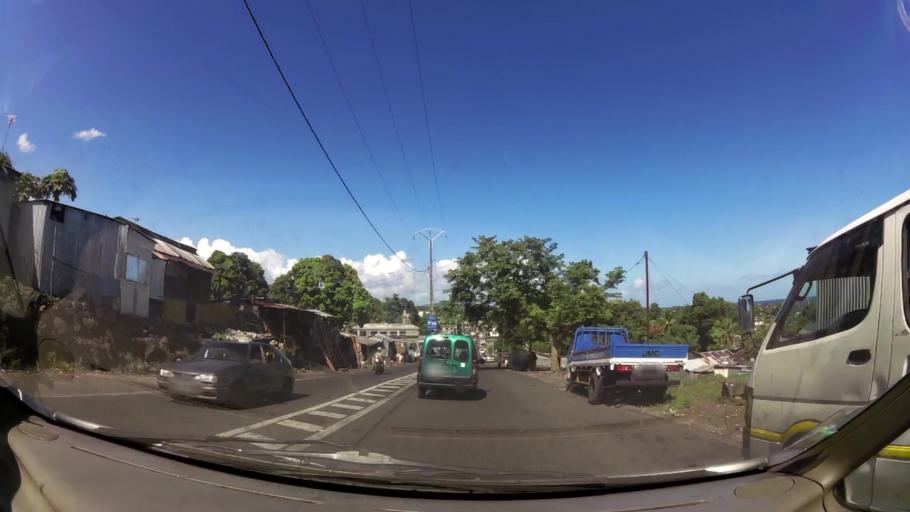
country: KM
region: Grande Comore
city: Moroni
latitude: -11.6983
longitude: 43.2564
